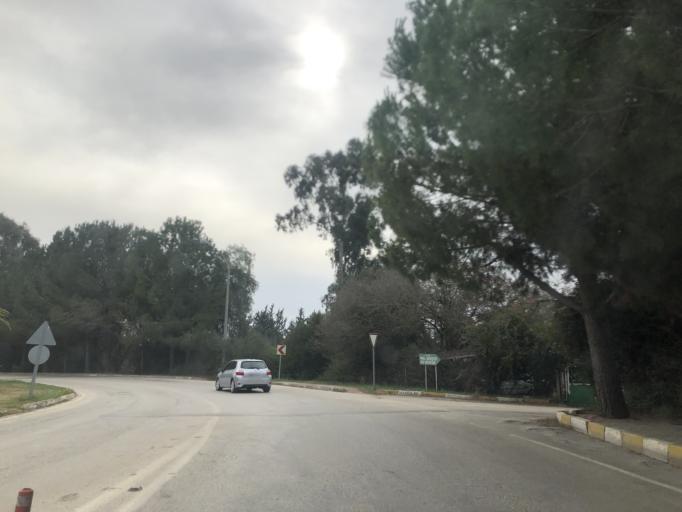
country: TR
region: Adana
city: Adana
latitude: 37.0567
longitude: 35.3541
